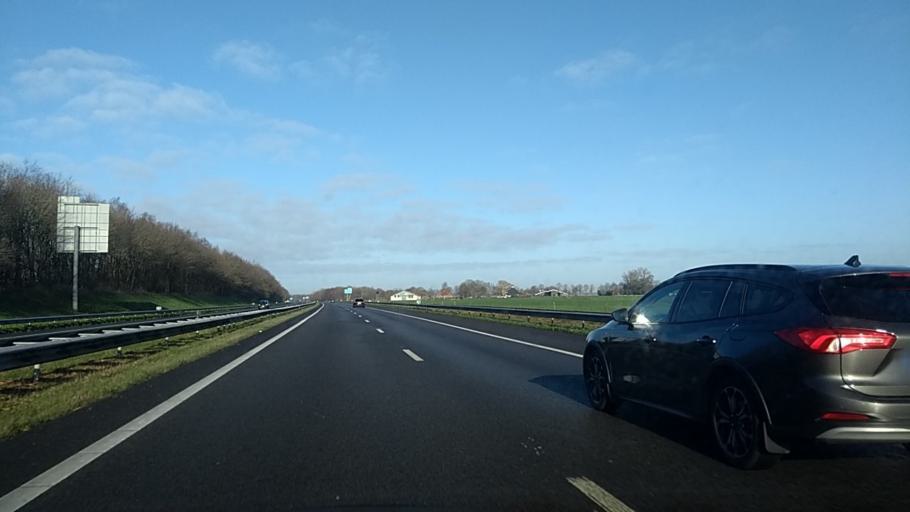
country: NL
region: Friesland
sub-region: Gemeente Weststellingwerf
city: Wolvega
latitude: 52.8936
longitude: 6.0180
